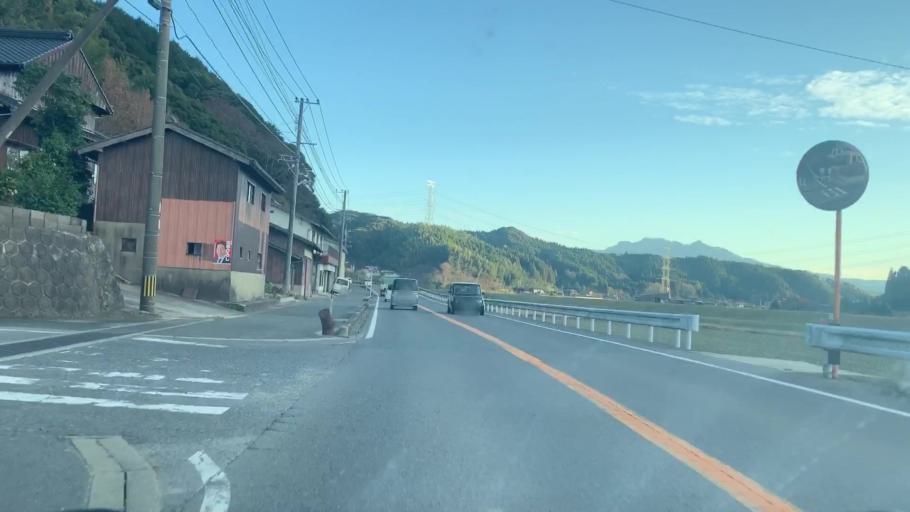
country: JP
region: Saga Prefecture
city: Karatsu
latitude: 33.3665
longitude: 130.0056
